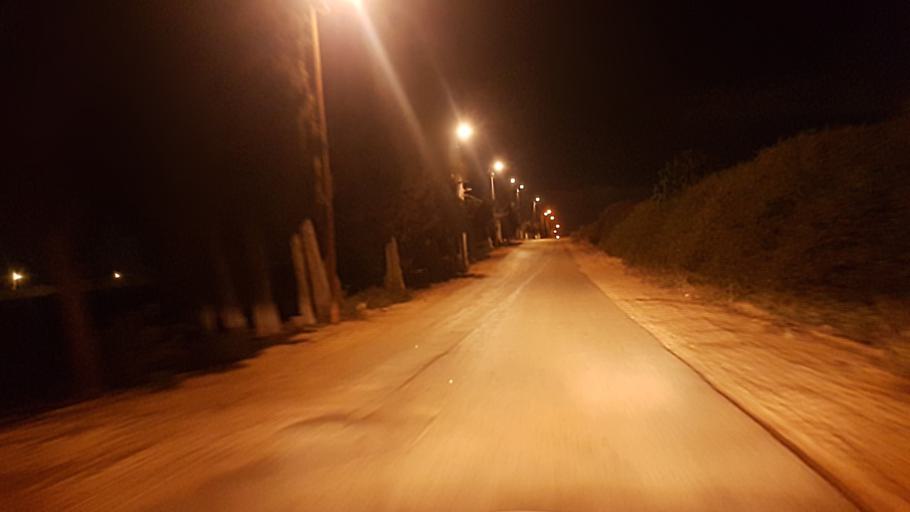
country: IL
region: Central District
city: Hod HaSharon
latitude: 32.1606
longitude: 34.8721
